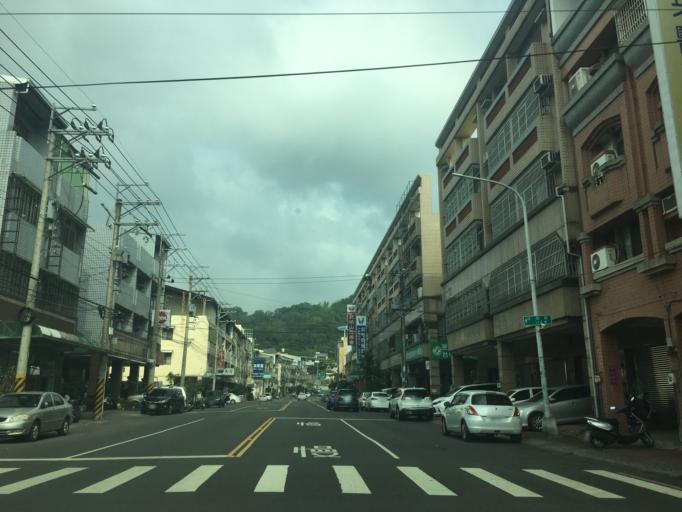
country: TW
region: Taiwan
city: Fengyuan
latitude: 24.2424
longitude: 120.7308
